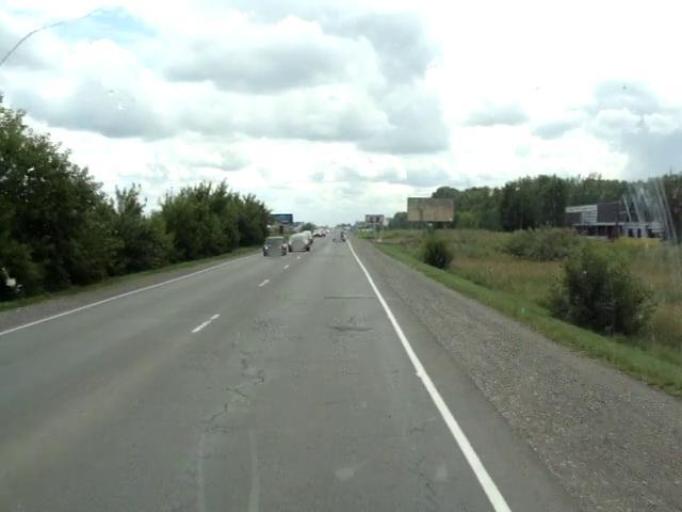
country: RU
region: Altai Krai
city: Zarya
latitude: 52.5736
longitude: 85.1819
